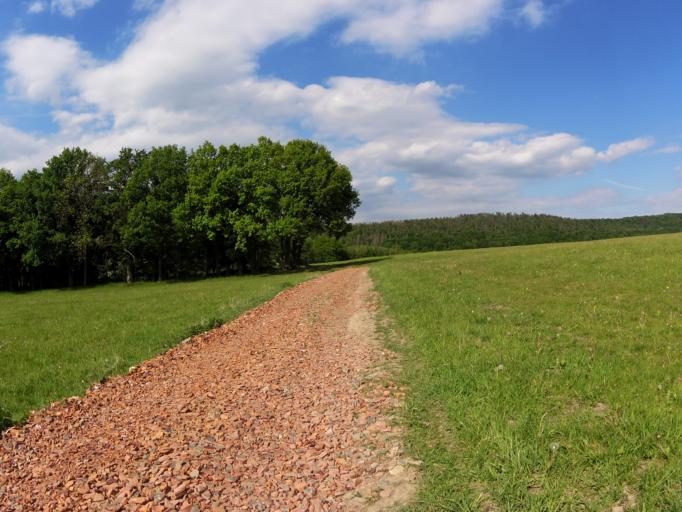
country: DE
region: Thuringia
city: Seebach
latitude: 50.9562
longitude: 10.4284
